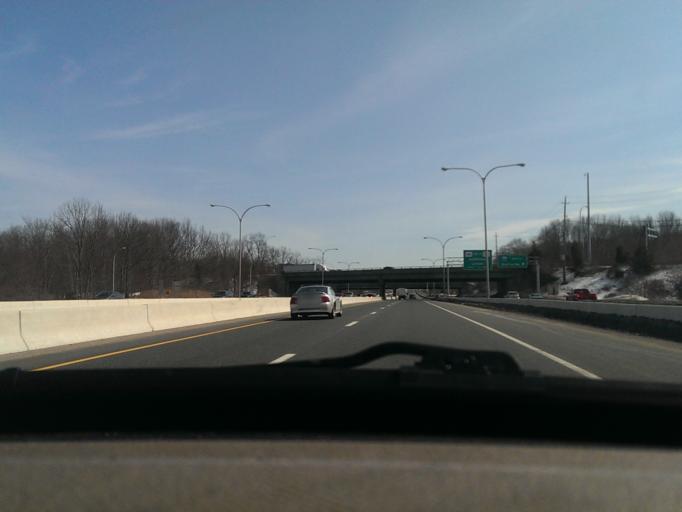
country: US
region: Rhode Island
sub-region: Providence County
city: Cumberland Hill
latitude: 41.9451
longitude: -71.4786
